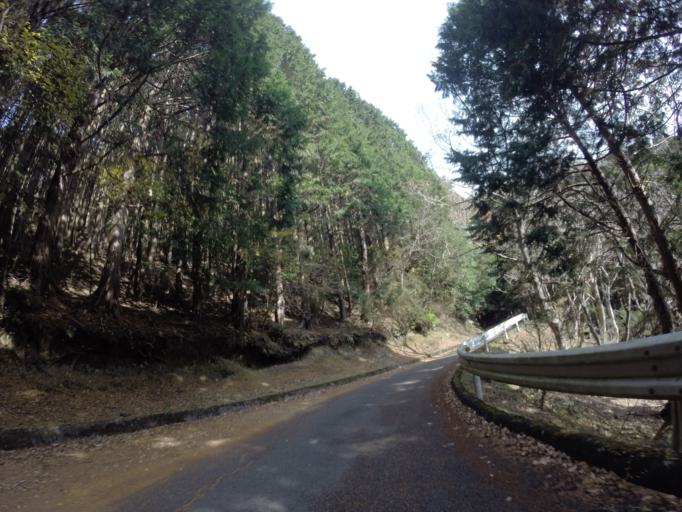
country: JP
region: Shizuoka
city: Heda
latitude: 34.8352
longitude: 138.8479
